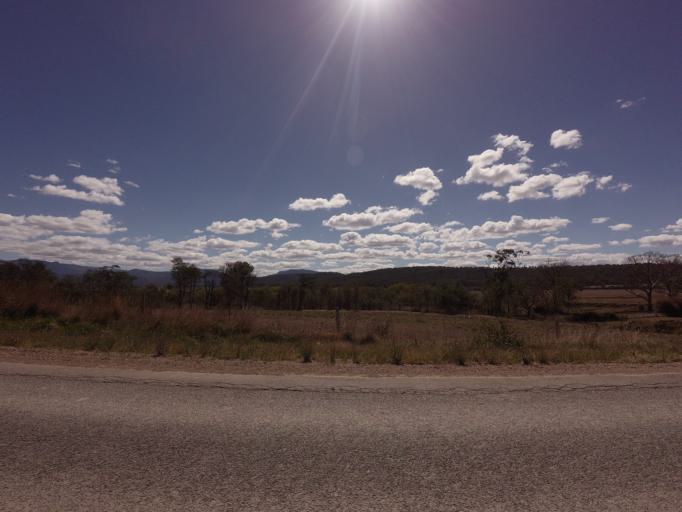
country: AU
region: Tasmania
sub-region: Break O'Day
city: St Helens
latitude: -41.6474
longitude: 147.9366
